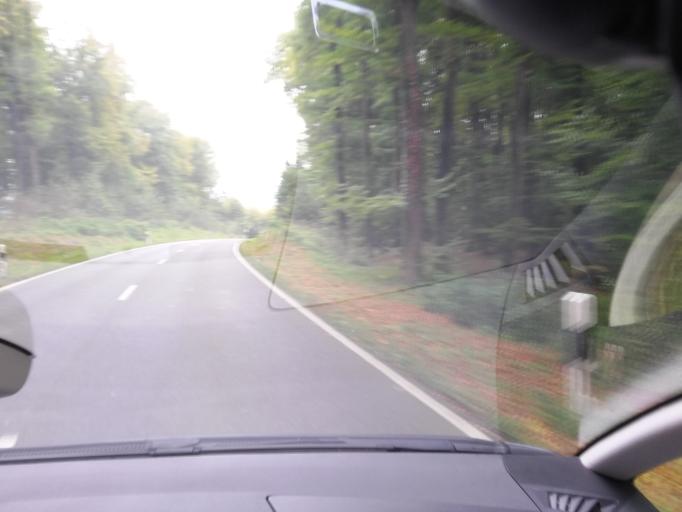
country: LU
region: Luxembourg
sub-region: Canton de Capellen
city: Hobscheid
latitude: 49.7139
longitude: 5.9141
